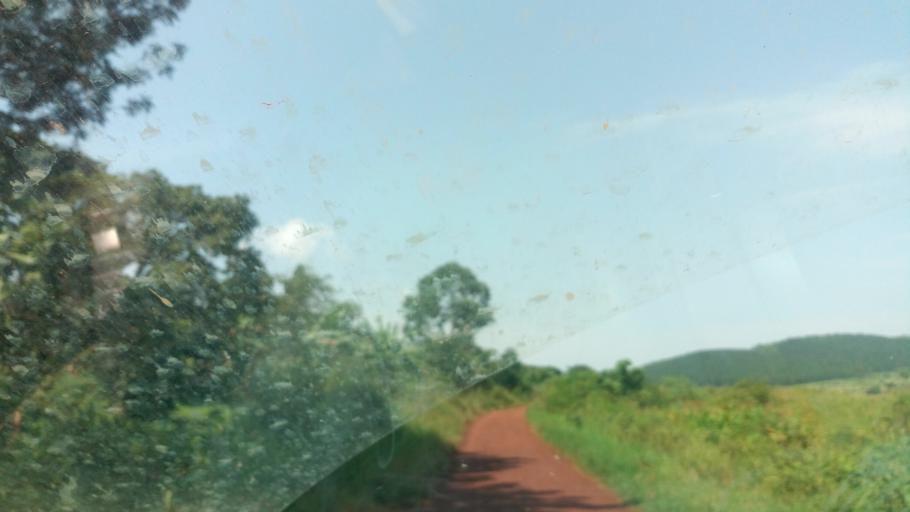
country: UG
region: Western Region
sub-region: Masindi District
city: Masindi
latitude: 1.6557
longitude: 31.8091
